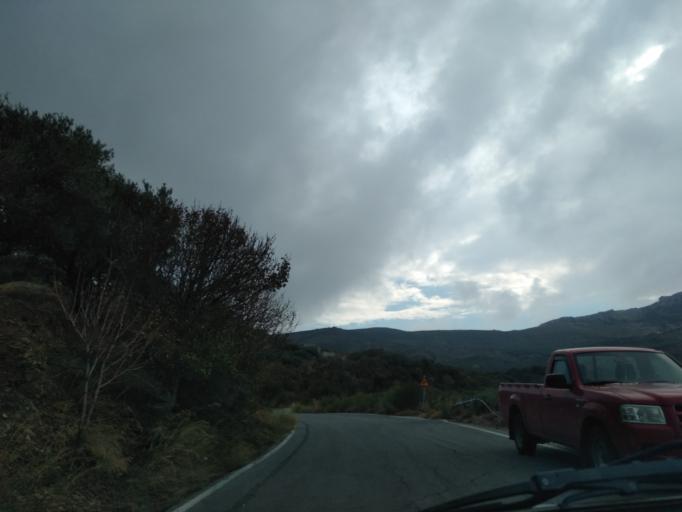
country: GR
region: Crete
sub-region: Nomos Lasithiou
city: Siteia
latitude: 35.1395
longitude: 26.0228
